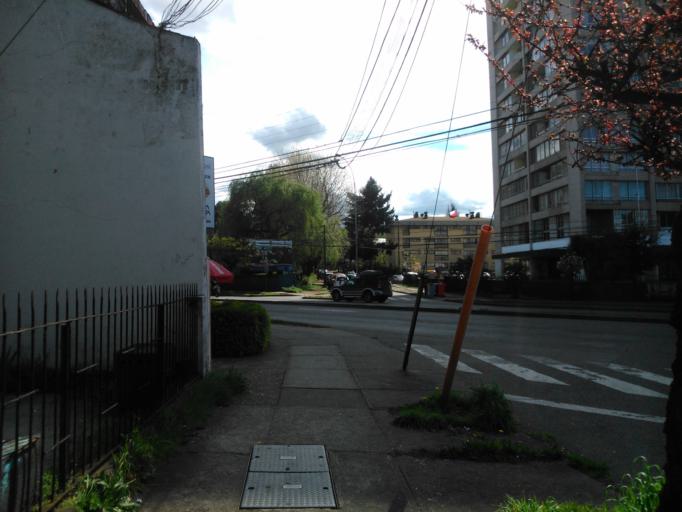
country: CL
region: Araucania
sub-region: Provincia de Cautin
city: Temuco
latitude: -38.7392
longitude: -72.5993
